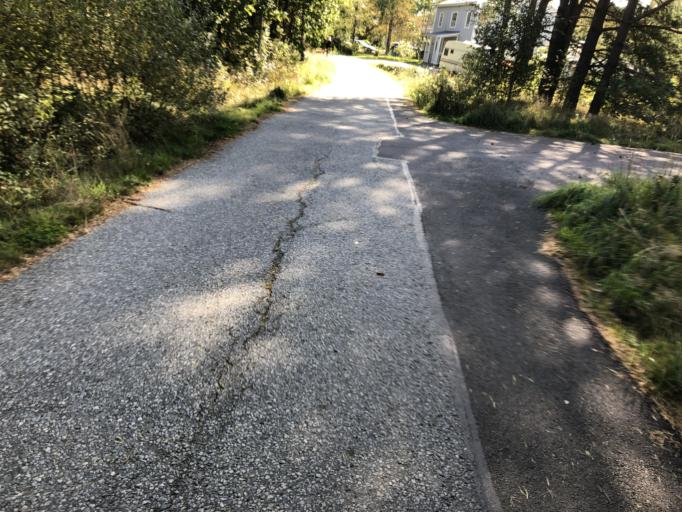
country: SE
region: Vaestra Goetaland
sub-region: Goteborg
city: Torslanda
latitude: 57.7379
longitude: 11.8345
